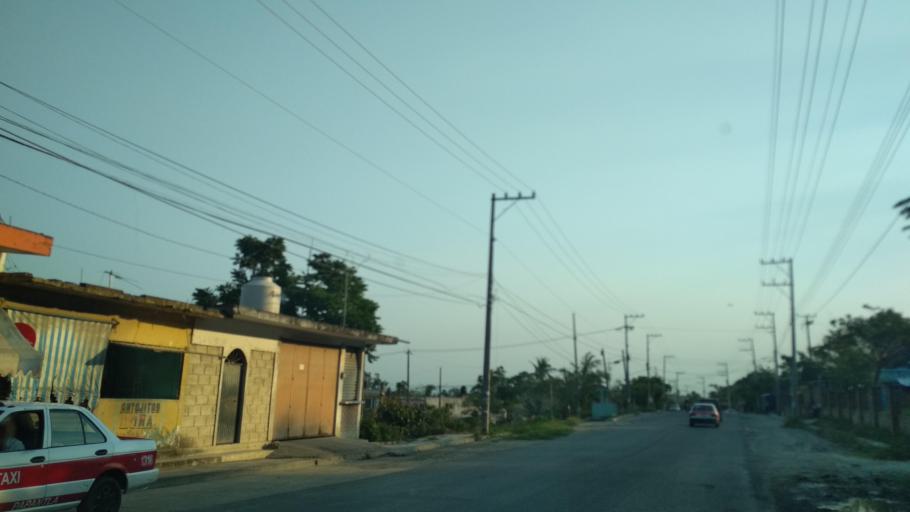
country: MM
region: Shan
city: Taunggyi
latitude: 20.4111
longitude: 97.3369
